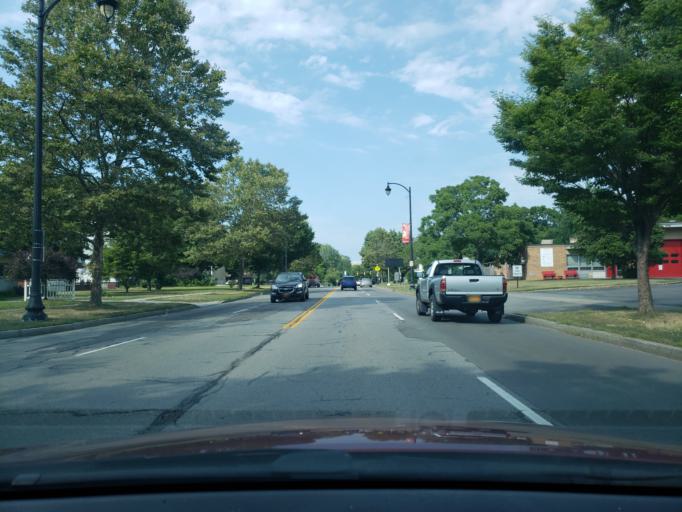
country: US
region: New York
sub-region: Monroe County
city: Irondequoit
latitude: 43.2443
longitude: -77.6184
